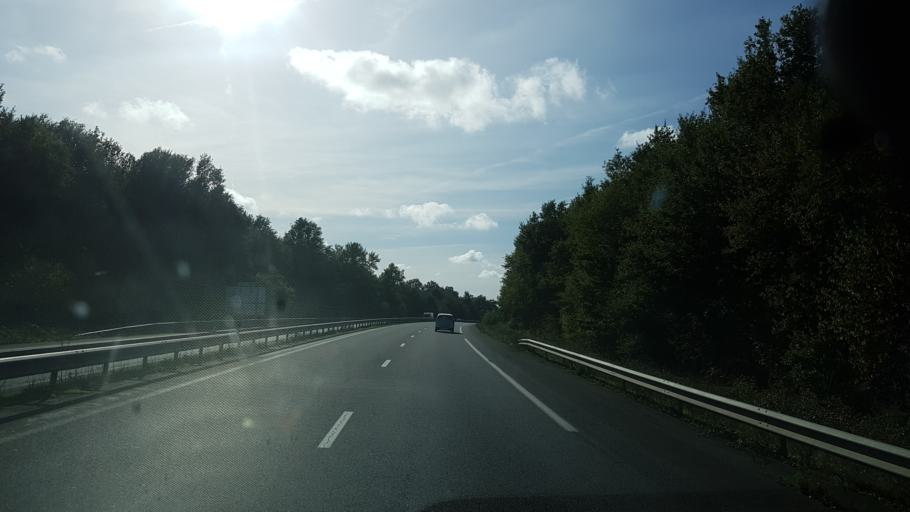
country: FR
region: Poitou-Charentes
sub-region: Departement de la Charente
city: Taponnat-Fleurignac
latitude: 45.7948
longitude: 0.4316
